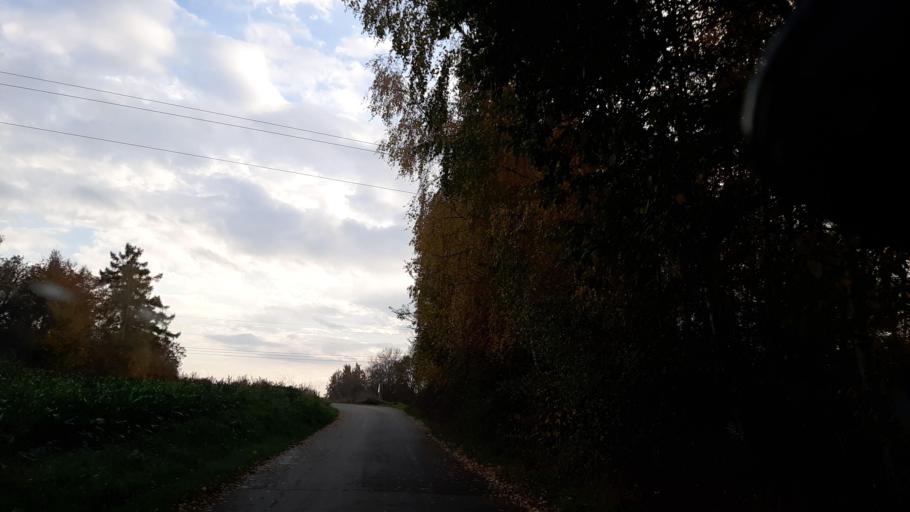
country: PL
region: Lublin Voivodeship
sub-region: Powiat lubelski
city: Garbow
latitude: 51.3435
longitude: 22.3190
